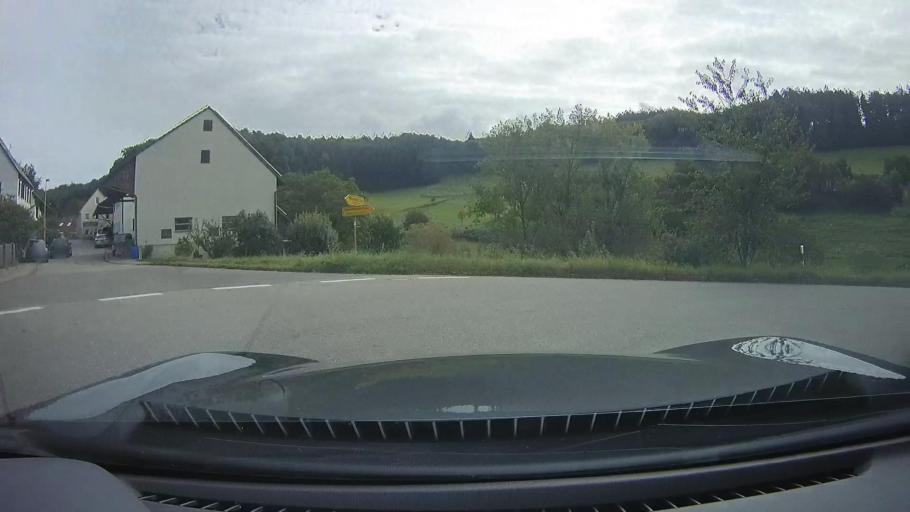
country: DE
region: Baden-Wuerttemberg
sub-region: Regierungsbezirk Stuttgart
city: Lowenstein
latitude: 49.0570
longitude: 9.3724
